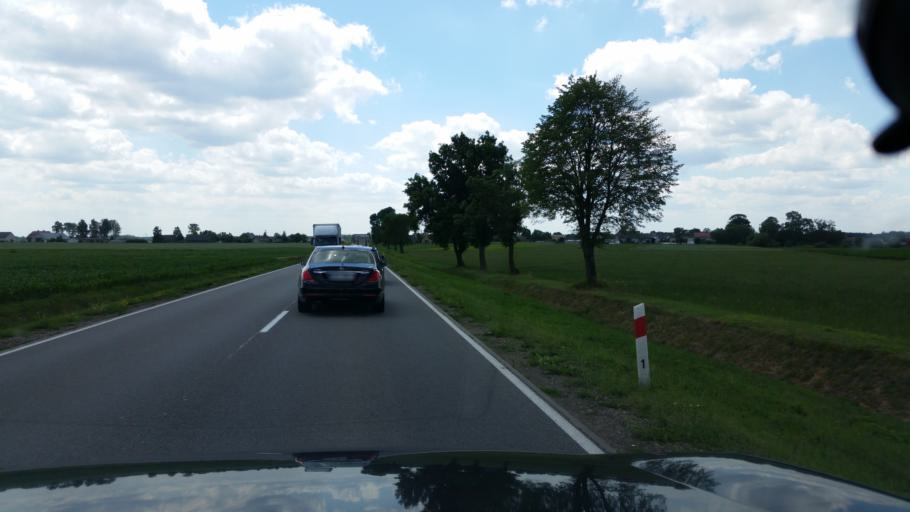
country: PL
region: Masovian Voivodeship
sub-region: Powiat ostrolecki
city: Czerwin
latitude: 52.9439
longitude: 21.8867
